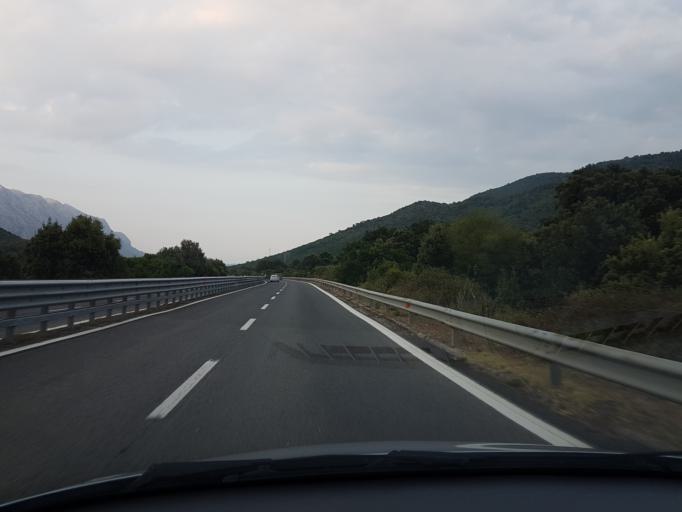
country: IT
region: Sardinia
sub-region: Provincia di Nuoro
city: Loculi
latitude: 40.4914
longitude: 9.6087
